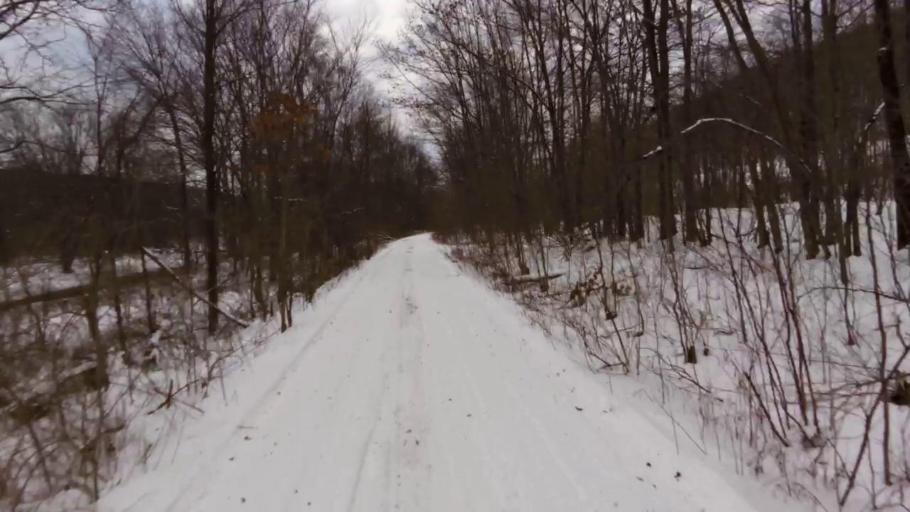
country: US
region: Pennsylvania
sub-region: McKean County
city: Foster Brook
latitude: 42.0573
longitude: -78.6374
